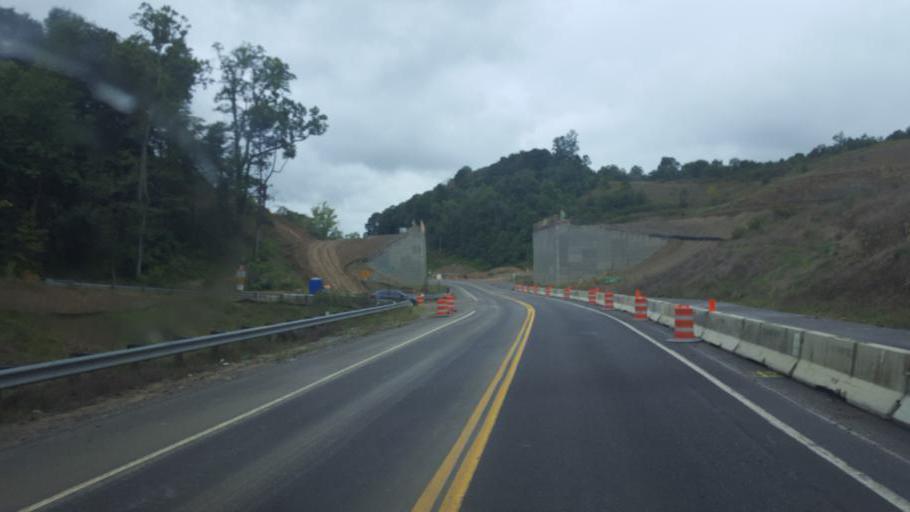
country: US
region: Ohio
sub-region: Scioto County
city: Sciotodale
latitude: 38.7544
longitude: -82.8715
